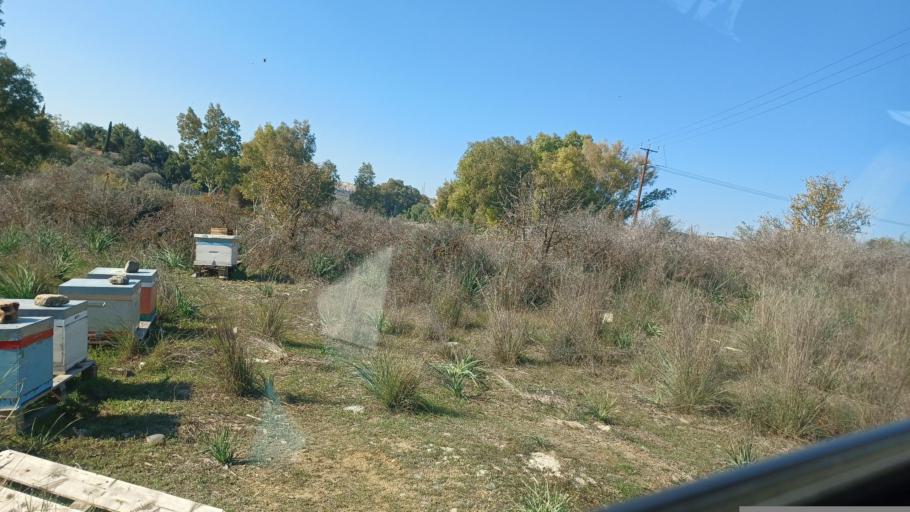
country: CY
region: Lefkosia
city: Alampra
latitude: 35.0201
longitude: 33.3783
